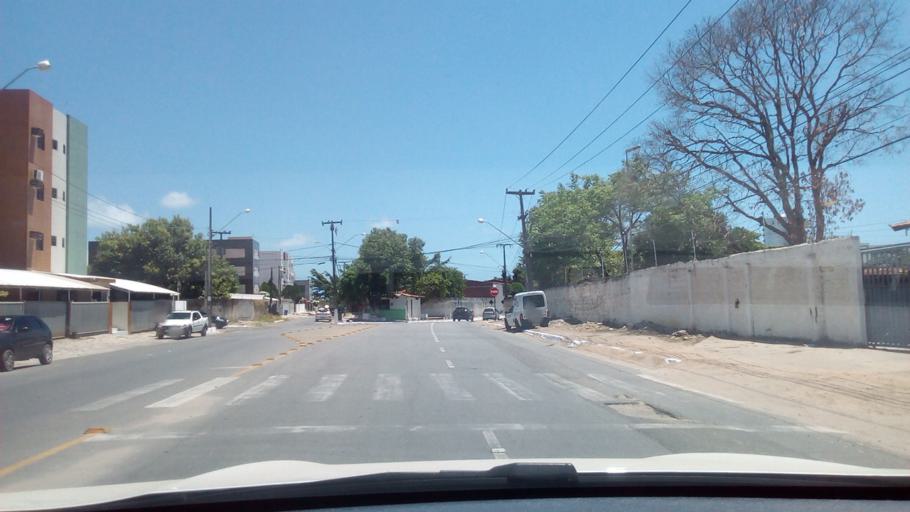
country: BR
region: Paraiba
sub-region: Joao Pessoa
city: Joao Pessoa
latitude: -7.1596
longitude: -34.8352
